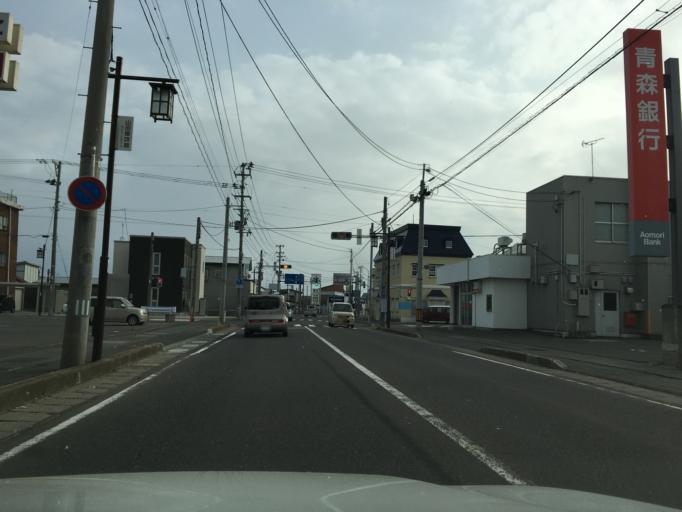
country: JP
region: Aomori
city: Namioka
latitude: 40.7120
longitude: 140.5901
